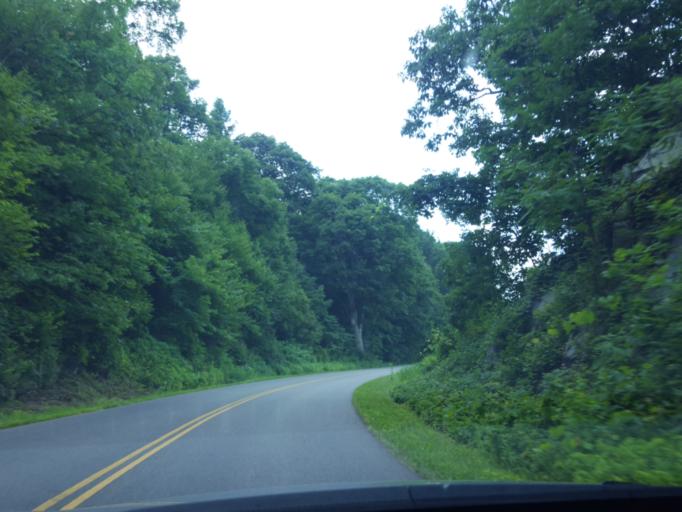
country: US
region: Virginia
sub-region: Nelson County
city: Nellysford
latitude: 37.9521
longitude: -78.9105
